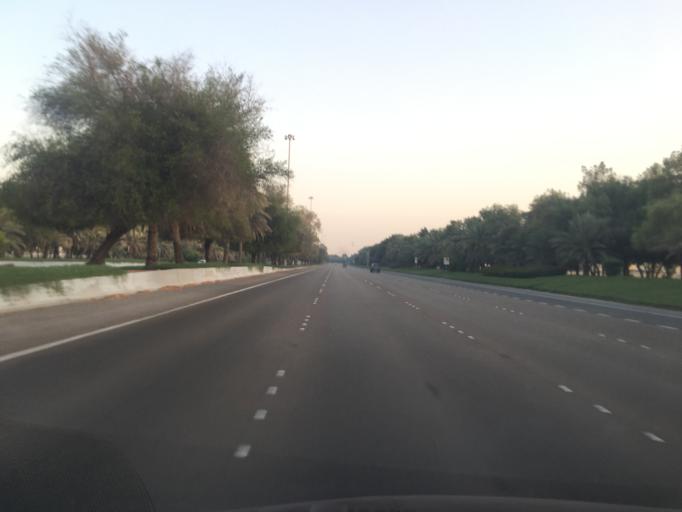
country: AE
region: Abu Dhabi
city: Abu Dhabi
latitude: 24.3988
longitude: 54.5313
